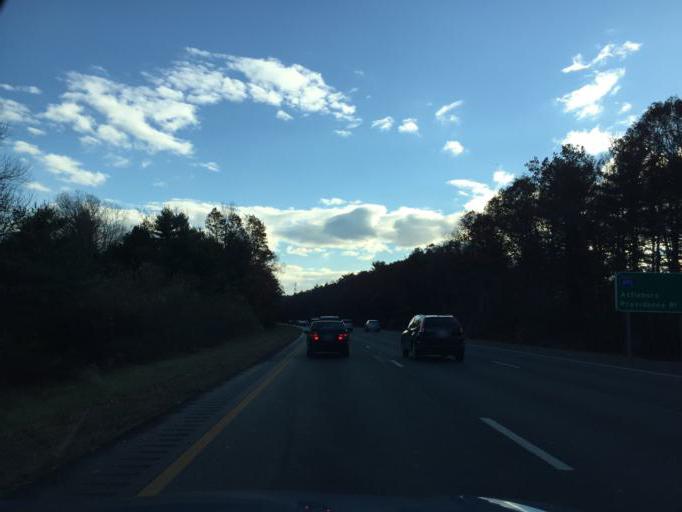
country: US
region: Massachusetts
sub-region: Norfolk County
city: Walpole
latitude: 42.1181
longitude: -71.2316
